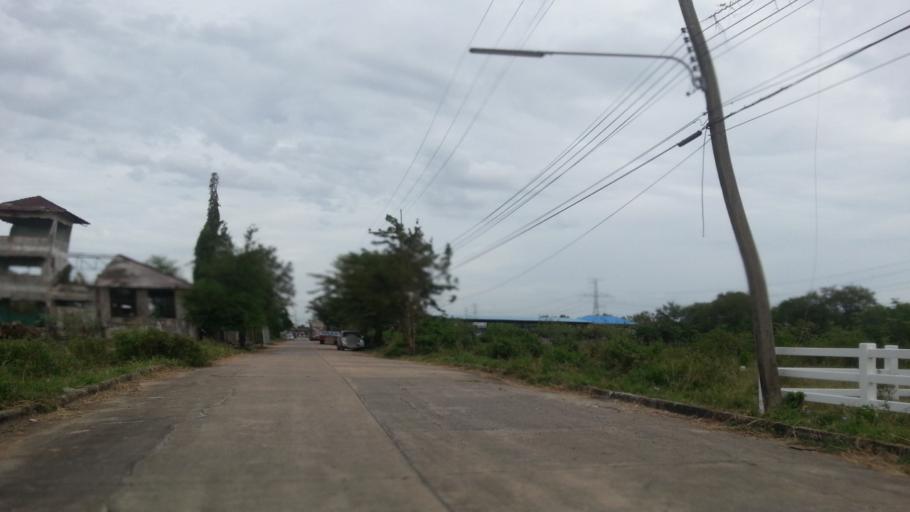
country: TH
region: Pathum Thani
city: Nong Suea
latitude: 14.0671
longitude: 100.8785
